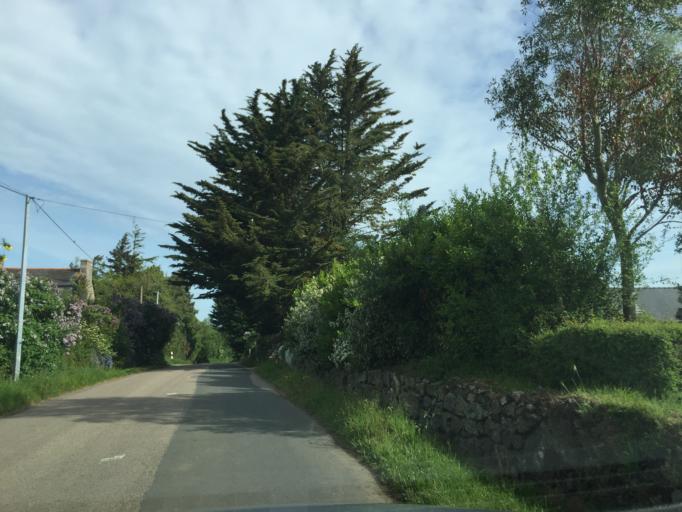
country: FR
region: Brittany
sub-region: Departement des Cotes-d'Armor
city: Matignon
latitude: 48.6421
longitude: -2.3239
